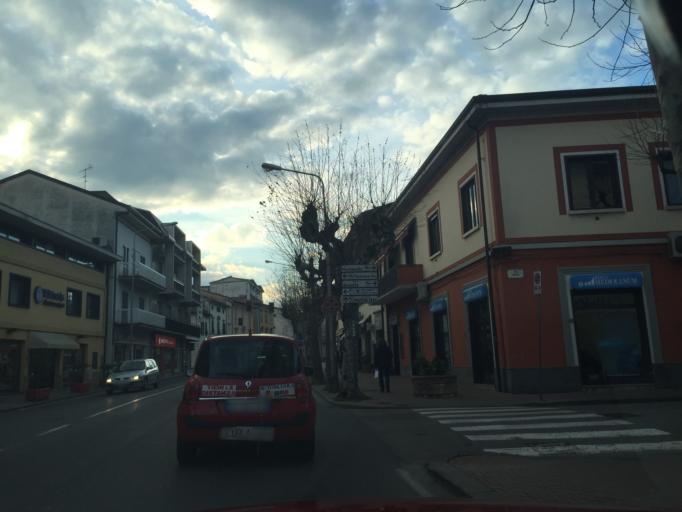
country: IT
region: Tuscany
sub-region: Provincia di Pistoia
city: Montecatini-Terme
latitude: 43.8808
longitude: 10.7765
